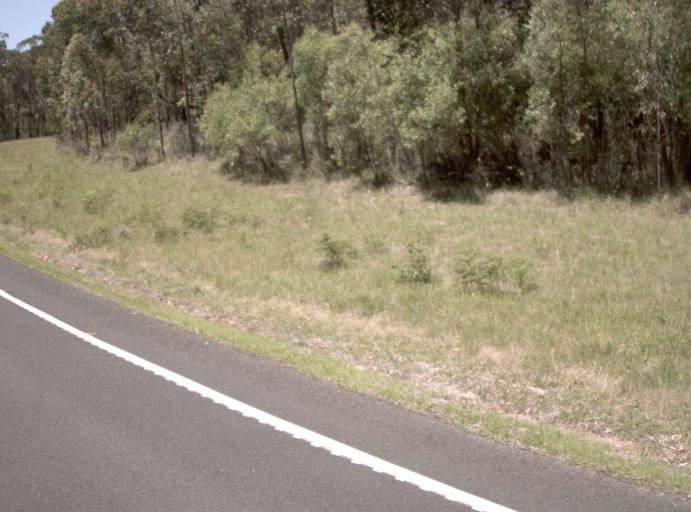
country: AU
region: Victoria
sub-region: East Gippsland
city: Lakes Entrance
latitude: -37.6960
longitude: 148.5896
